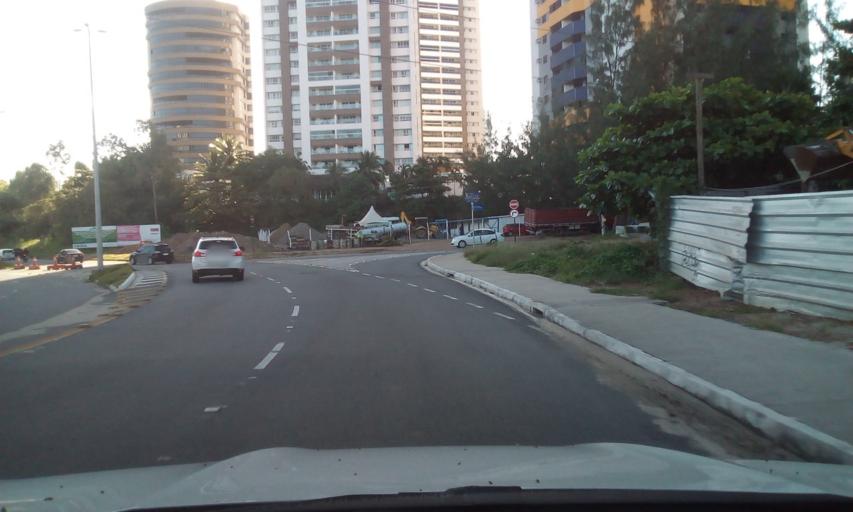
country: BR
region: Paraiba
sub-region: Joao Pessoa
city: Joao Pessoa
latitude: -7.1244
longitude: -34.8306
